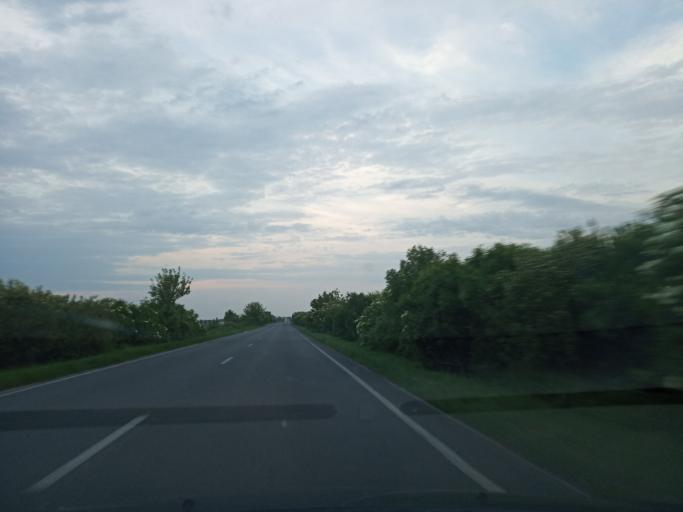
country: RO
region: Timis
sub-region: Comuna Voiteg
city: Voiteg
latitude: 45.4508
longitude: 21.2336
